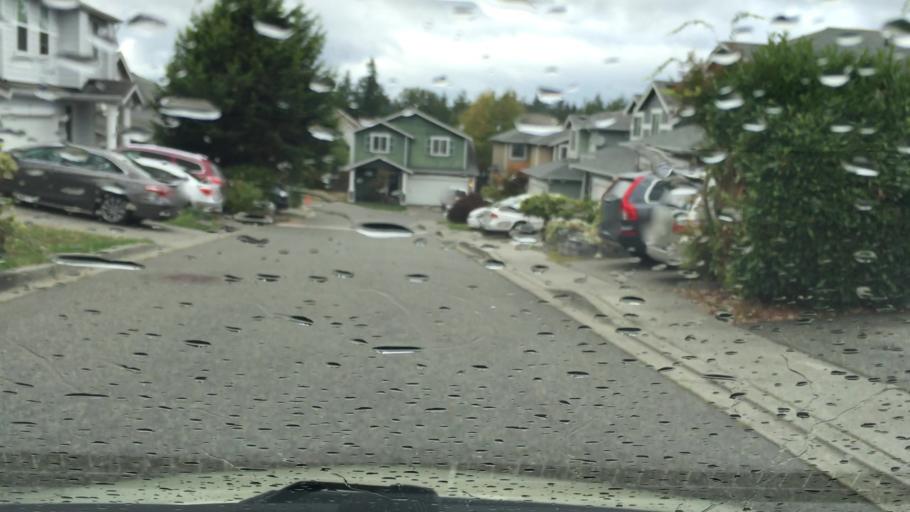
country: US
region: Washington
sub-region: Snohomish County
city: Martha Lake
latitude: 47.8838
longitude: -122.2505
